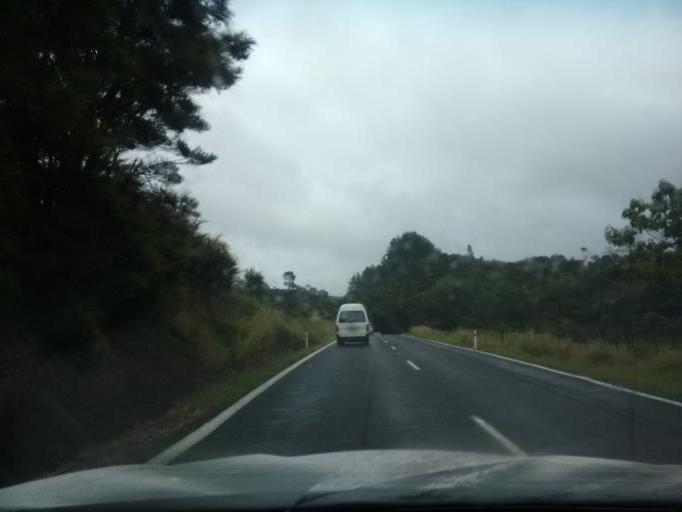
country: NZ
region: Waikato
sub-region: Thames-Coromandel District
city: Whitianga
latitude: -36.9185
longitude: 175.6842
